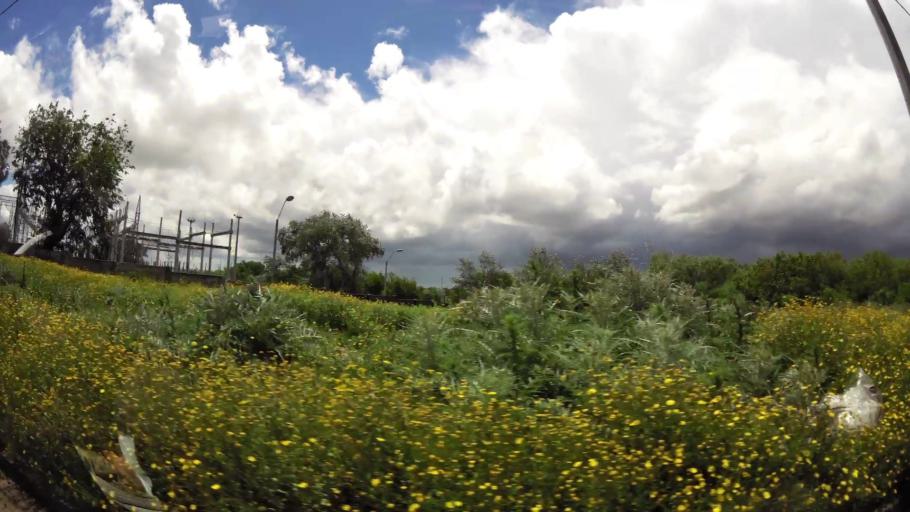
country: UY
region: Montevideo
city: Montevideo
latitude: -34.8366
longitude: -56.1829
